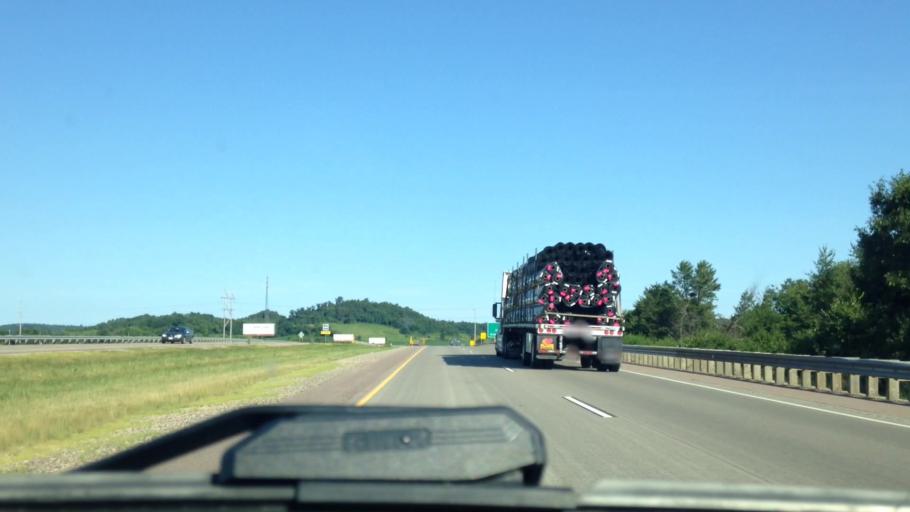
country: US
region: Wisconsin
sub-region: Jackson County
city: Black River Falls
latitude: 44.3853
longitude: -90.9988
